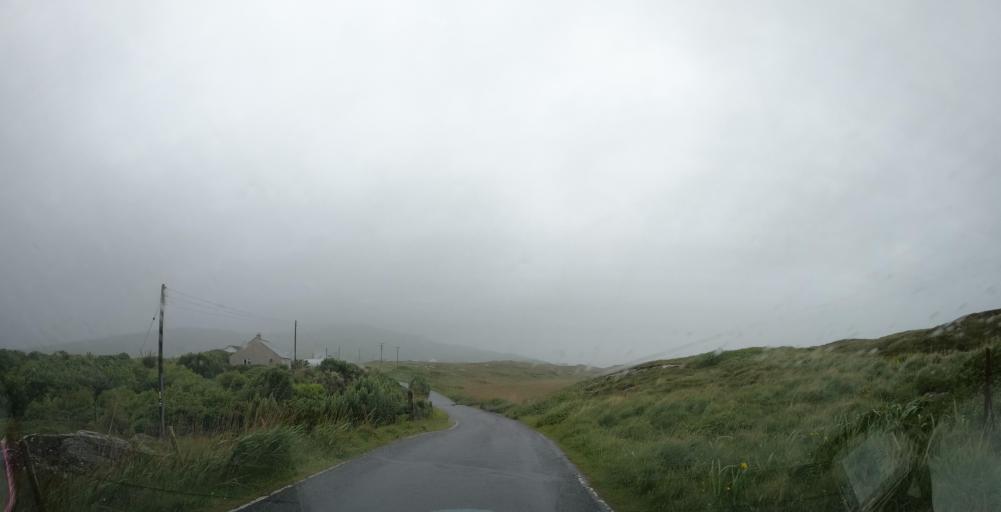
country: GB
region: Scotland
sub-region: Eilean Siar
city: Barra
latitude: 57.0087
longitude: -7.4169
